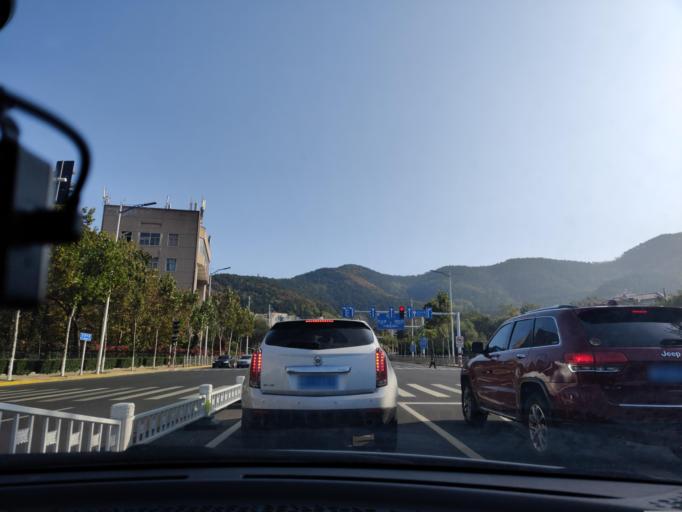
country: CN
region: Shandong Sheng
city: Xiangyang
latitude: 37.5198
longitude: 121.3979
